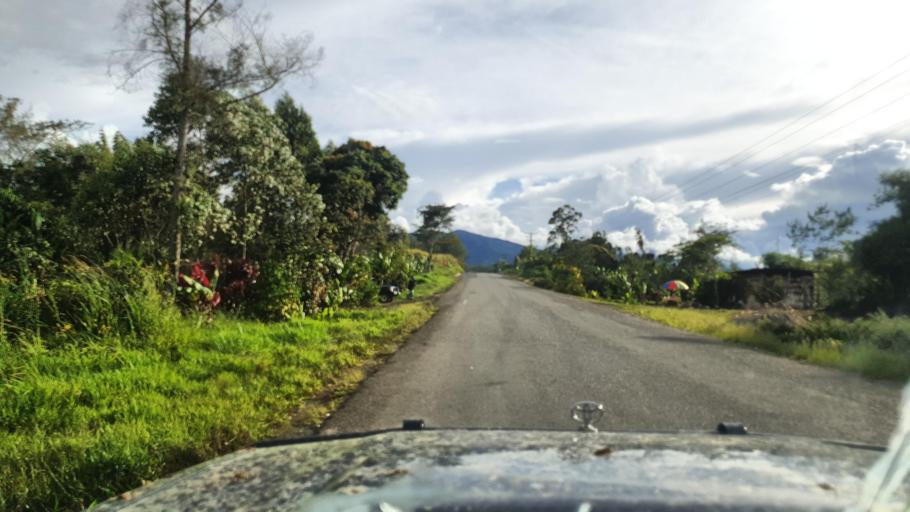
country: PG
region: Jiwaka
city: Minj
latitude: -5.8798
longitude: 144.6897
